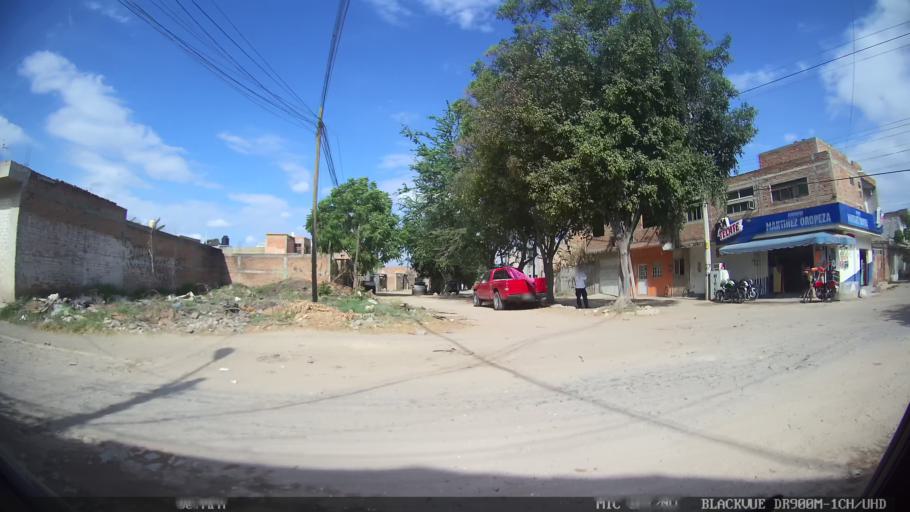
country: MX
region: Jalisco
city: Tonala
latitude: 20.6621
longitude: -103.2532
